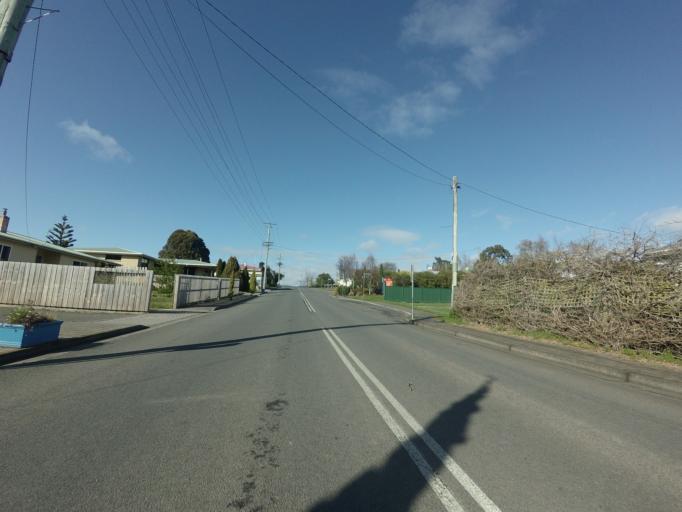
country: AU
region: Tasmania
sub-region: Huon Valley
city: Cygnet
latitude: -43.3126
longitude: 147.0155
